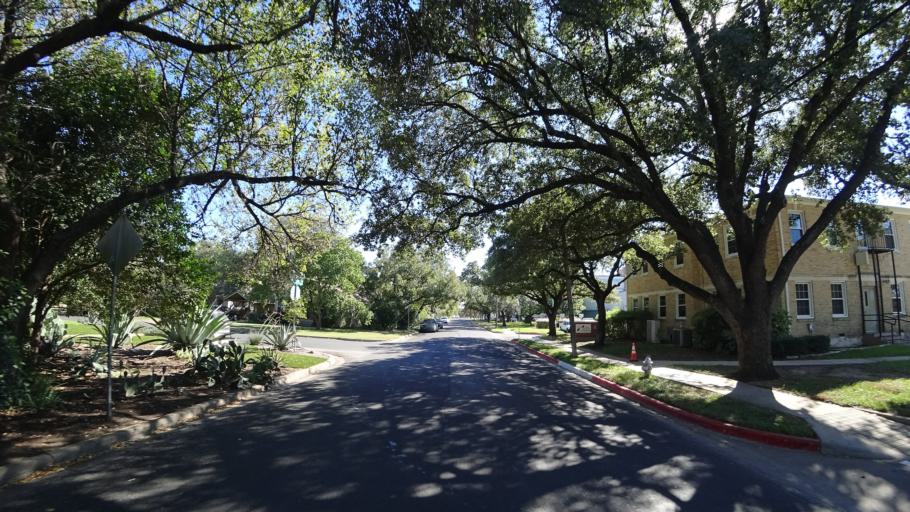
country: US
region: Texas
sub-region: Travis County
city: Austin
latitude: 30.3129
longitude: -97.7554
